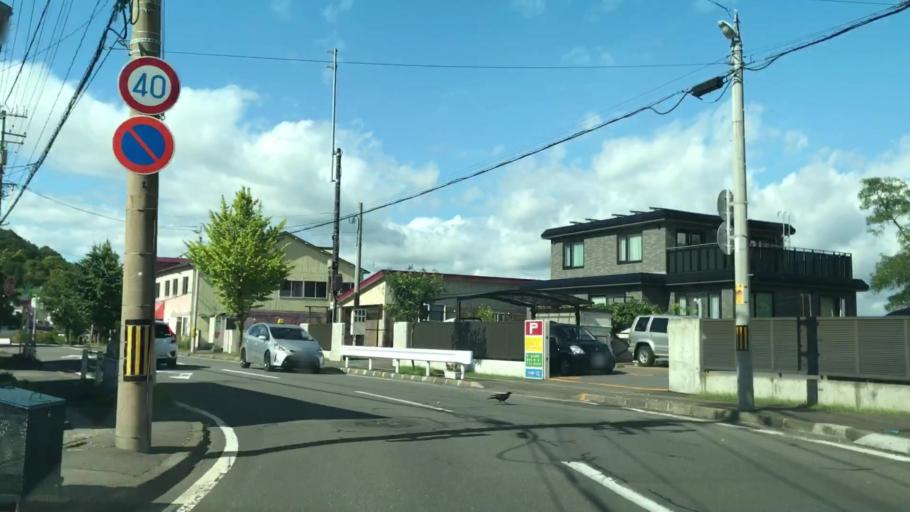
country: JP
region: Hokkaido
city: Muroran
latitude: 42.3248
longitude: 140.9678
